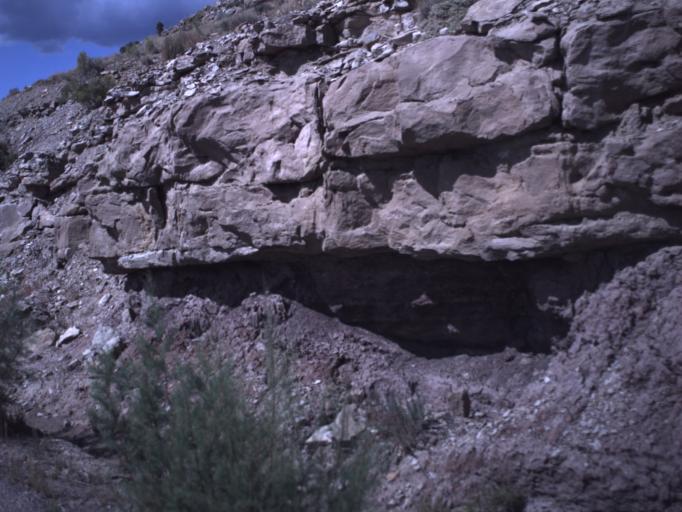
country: US
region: Utah
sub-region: Duchesne County
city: Duchesne
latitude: 40.1743
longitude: -110.4416
